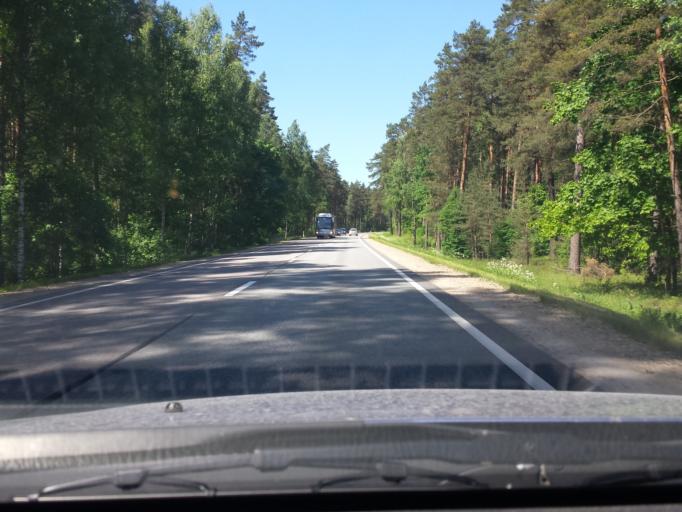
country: LV
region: Riga
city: Bergi
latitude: 56.9917
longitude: 24.3138
